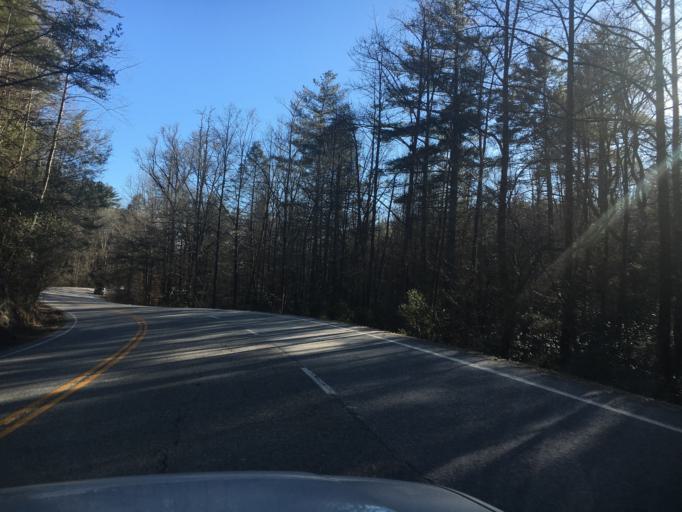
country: US
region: Georgia
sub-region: Lumpkin County
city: Dahlonega
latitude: 34.6957
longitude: -83.9130
